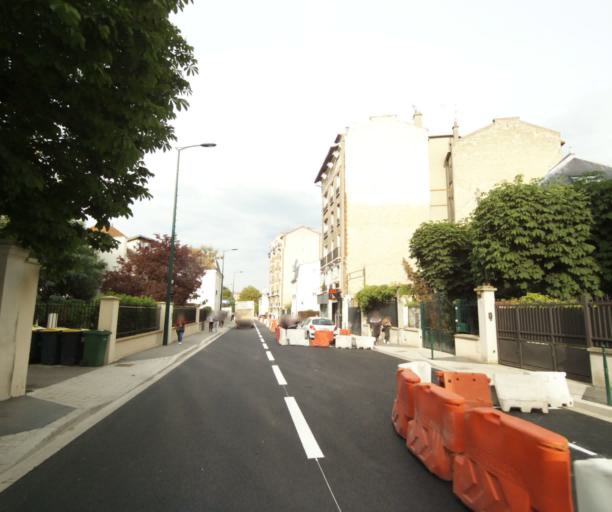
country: FR
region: Ile-de-France
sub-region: Departement des Hauts-de-Seine
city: Clichy
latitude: 48.8814
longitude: 2.3073
